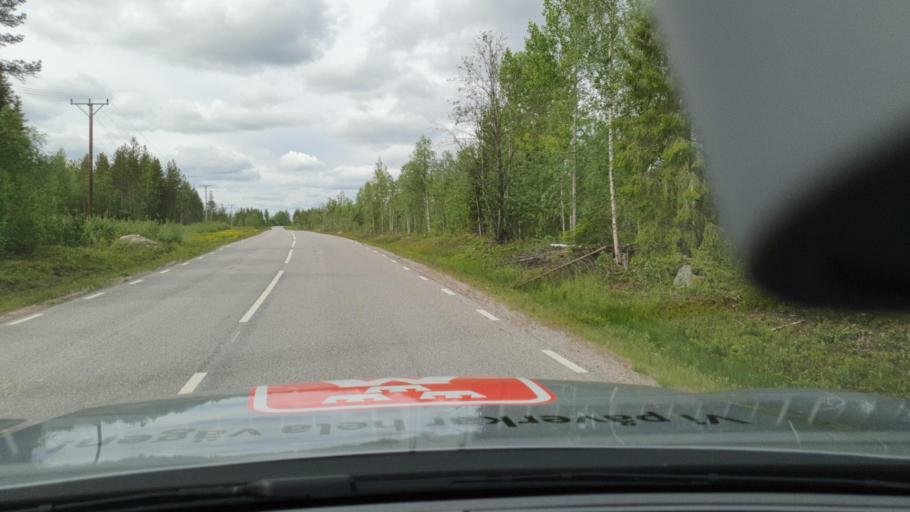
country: FI
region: Lapland
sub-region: Torniolaakso
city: Ylitornio
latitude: 66.0449
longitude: 23.6013
